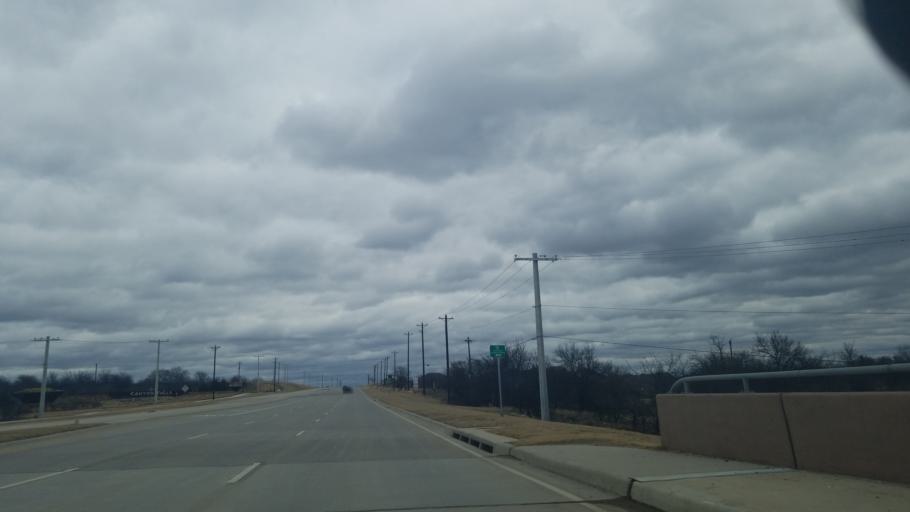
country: US
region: Texas
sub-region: Denton County
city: Roanoke
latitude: 33.0613
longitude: -97.2202
